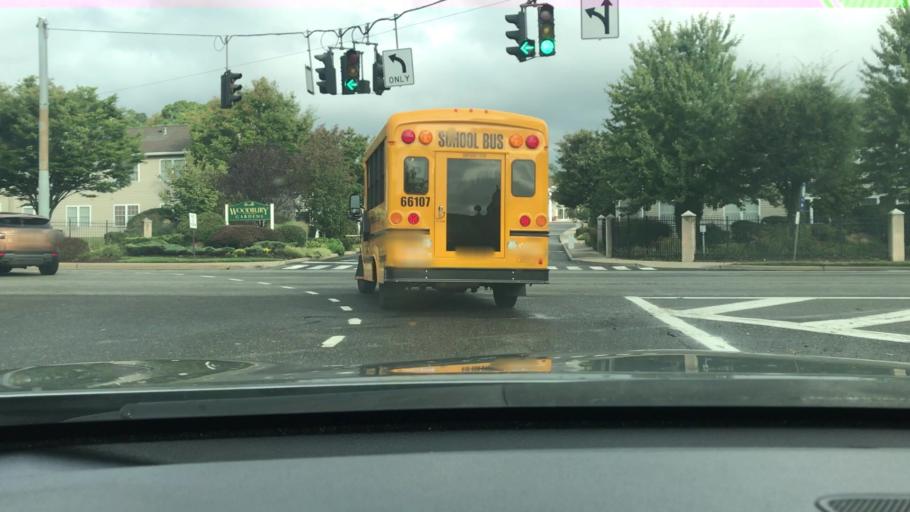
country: US
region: New York
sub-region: Nassau County
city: Syosset
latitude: 40.8125
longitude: -73.4868
